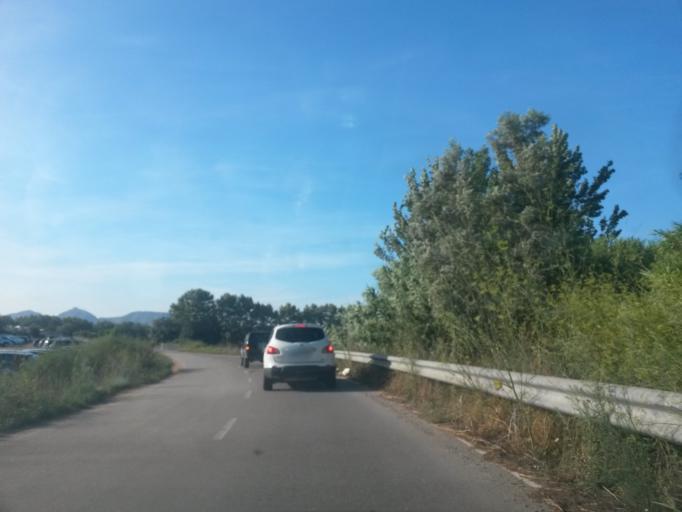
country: ES
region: Catalonia
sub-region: Provincia de Girona
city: Pals
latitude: 42.0007
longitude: 3.1692
